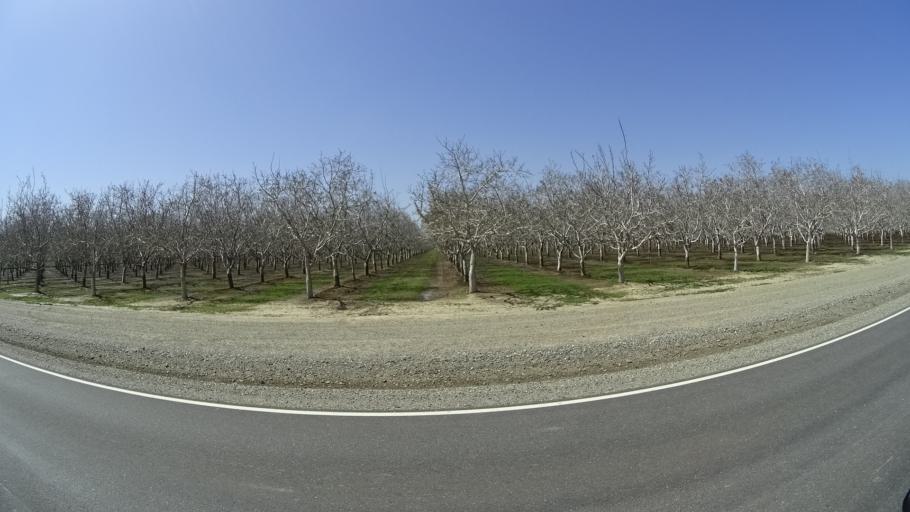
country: US
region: California
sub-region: Glenn County
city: Willows
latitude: 39.6094
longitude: -122.1376
